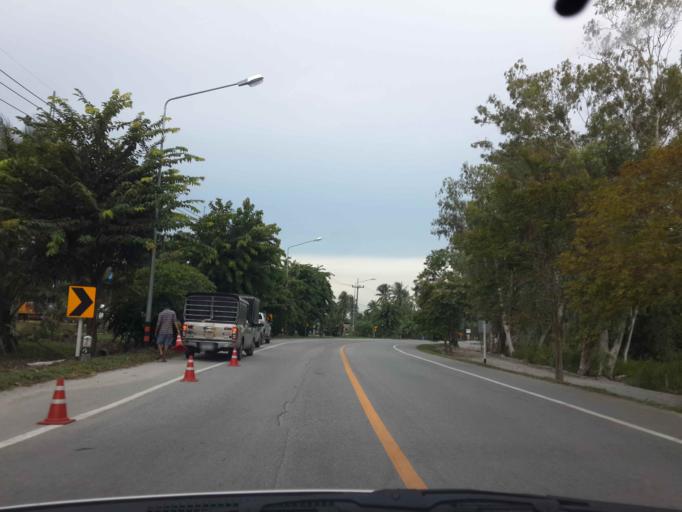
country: TH
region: Chon Buri
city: Si Racha
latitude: 13.2371
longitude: 100.9881
